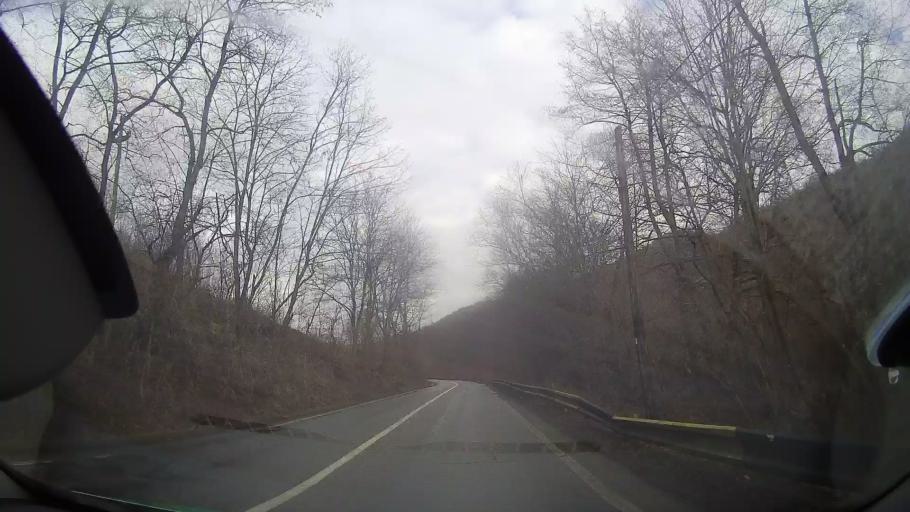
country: RO
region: Alba
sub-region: Comuna Ocolis
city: Ocolis
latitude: 46.4468
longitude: 23.4687
